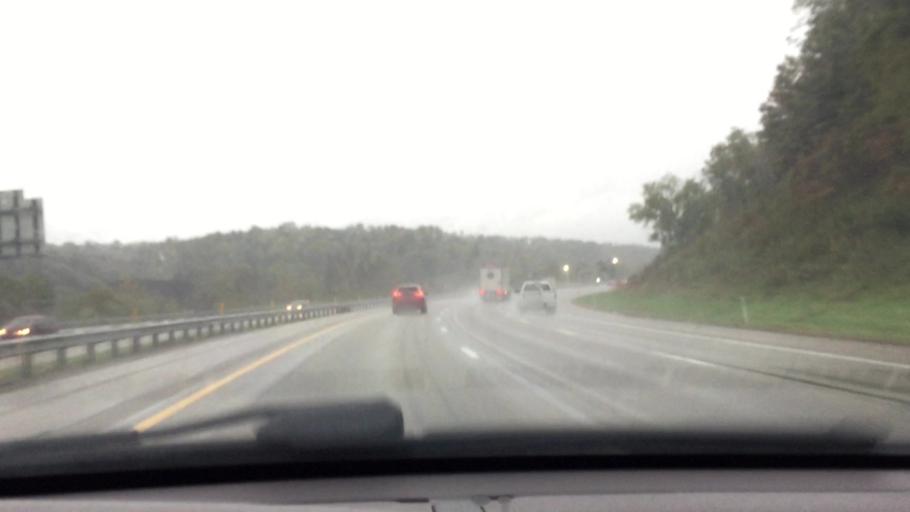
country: US
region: Pennsylvania
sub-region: Allegheny County
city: Bridgeville
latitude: 40.3692
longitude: -80.1185
